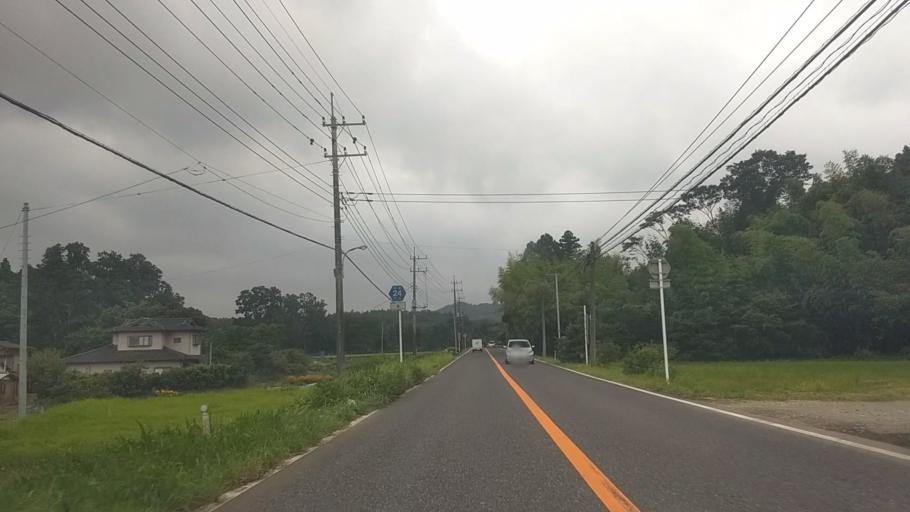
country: JP
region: Chiba
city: Kawaguchi
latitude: 35.2154
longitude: 140.0713
